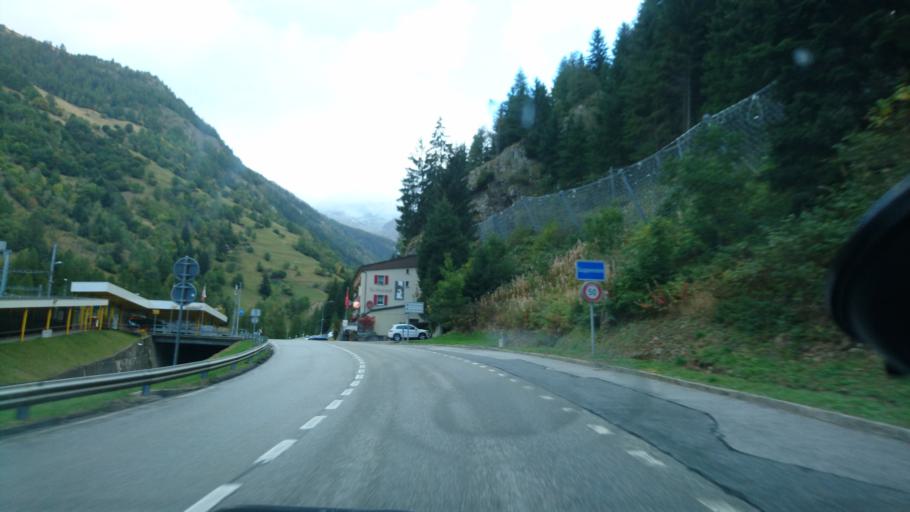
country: CH
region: Valais
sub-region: Leuk District
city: Gampel
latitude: 46.3672
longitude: 7.7562
